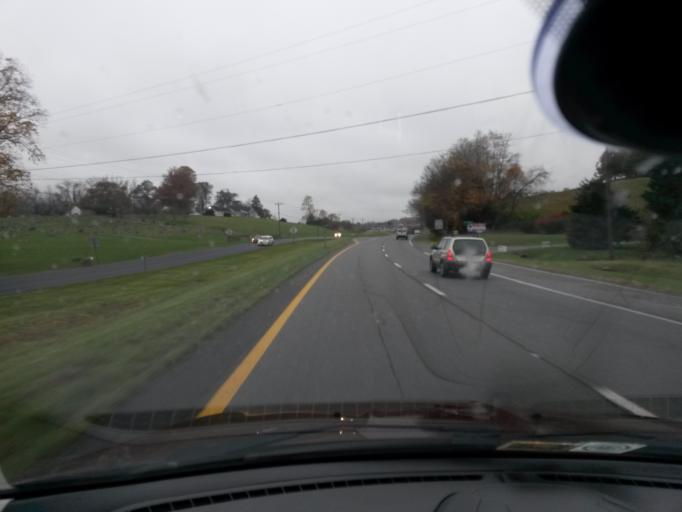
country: US
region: Virginia
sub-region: Botetourt County
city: Daleville
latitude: 37.3978
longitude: -79.9093
